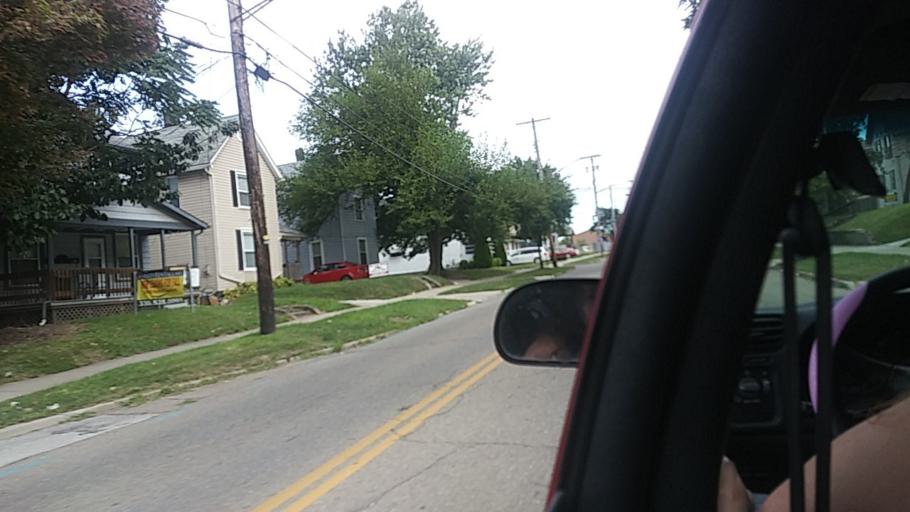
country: US
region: Ohio
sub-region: Summit County
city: Akron
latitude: 41.0676
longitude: -81.5098
